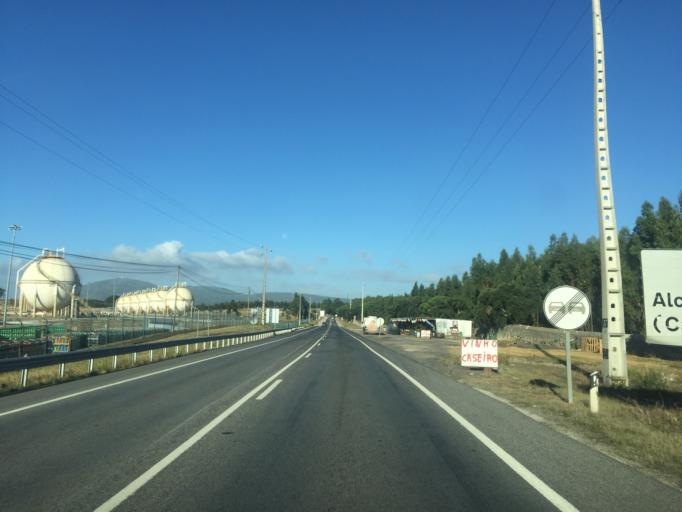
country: PT
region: Lisbon
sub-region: Azambuja
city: Aveiras de Cima
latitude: 39.1716
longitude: -8.9267
